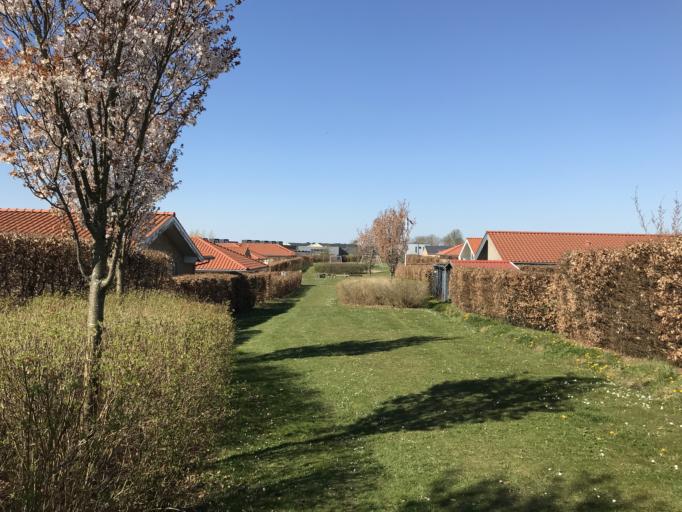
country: DK
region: Capital Region
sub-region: Hoje-Taastrup Kommune
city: Flong
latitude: 55.6606
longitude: 12.1527
